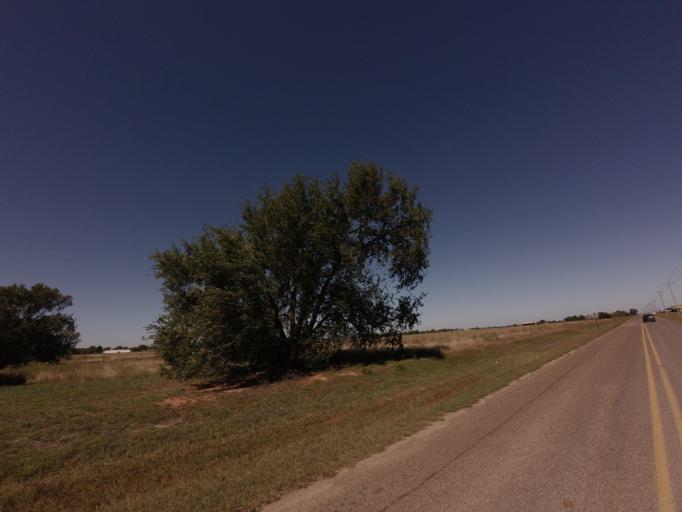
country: US
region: New Mexico
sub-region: Curry County
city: Clovis
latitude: 34.4196
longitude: -103.1609
